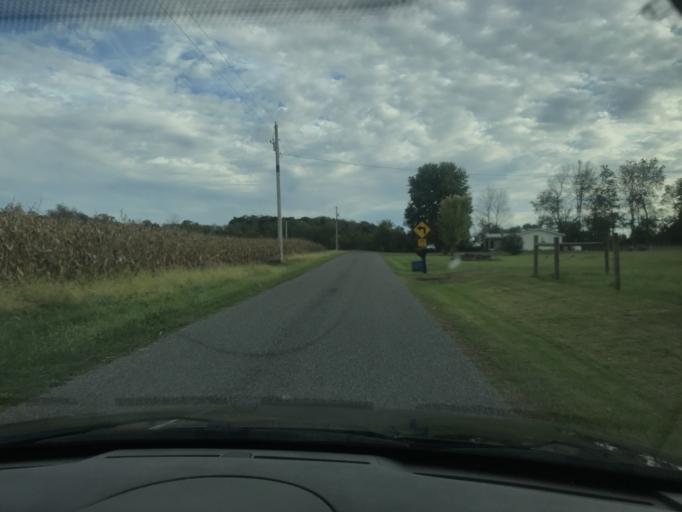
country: US
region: Ohio
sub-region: Logan County
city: West Liberty
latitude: 40.2491
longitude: -83.6948
